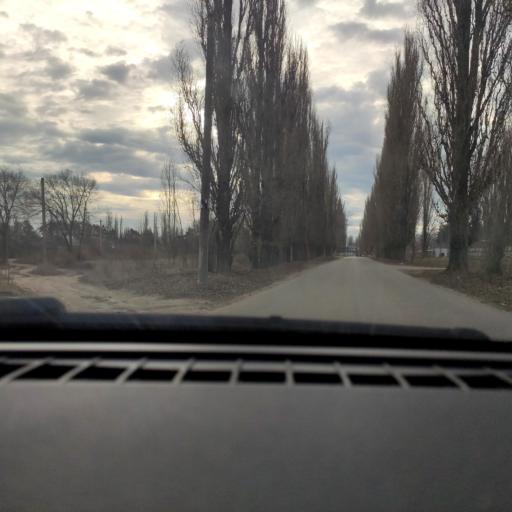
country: RU
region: Voronezj
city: Maslovka
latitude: 51.6001
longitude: 39.2207
